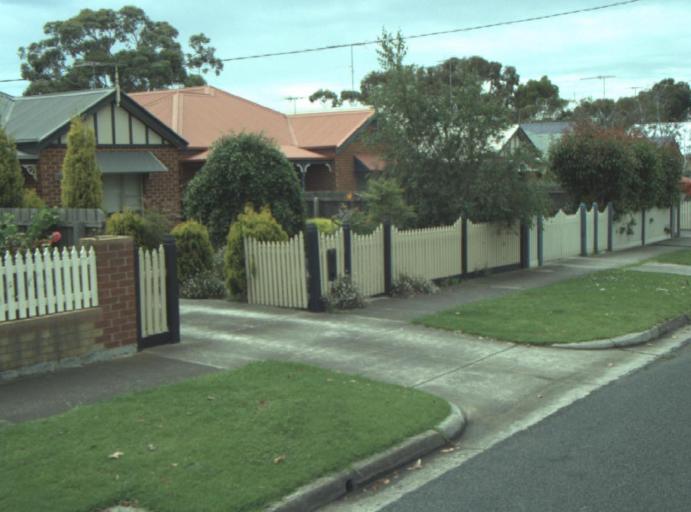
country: AU
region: Victoria
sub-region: Greater Geelong
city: East Geelong
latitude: -38.1660
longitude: 144.3745
